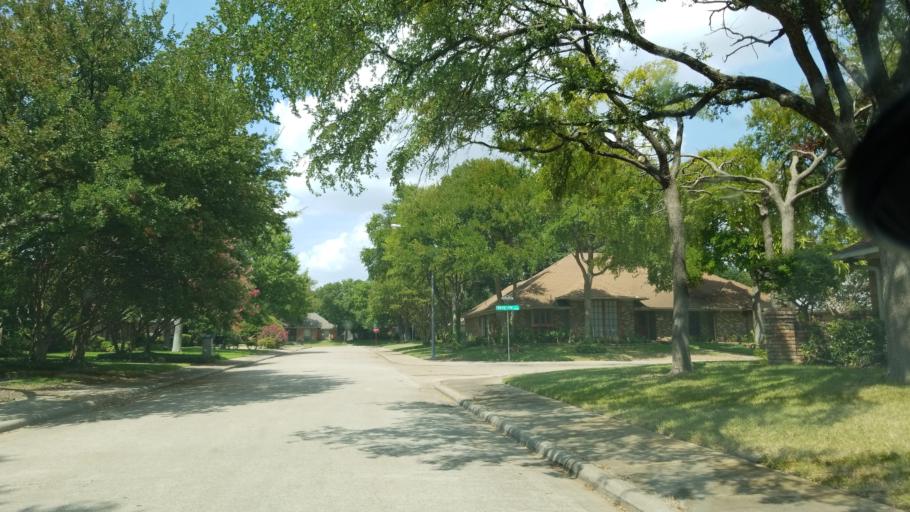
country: US
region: Texas
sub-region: Dallas County
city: Richardson
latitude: 32.9152
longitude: -96.7211
